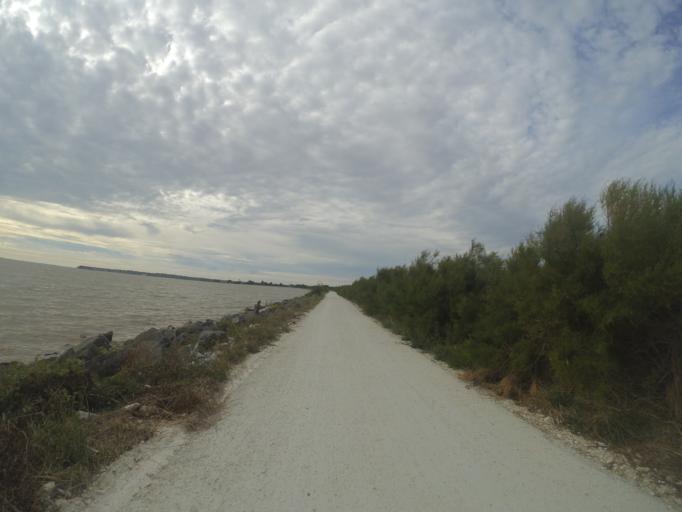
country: FR
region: Poitou-Charentes
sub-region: Departement de la Charente-Maritime
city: Meschers-sur-Gironde
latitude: 45.5456
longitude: -0.9115
